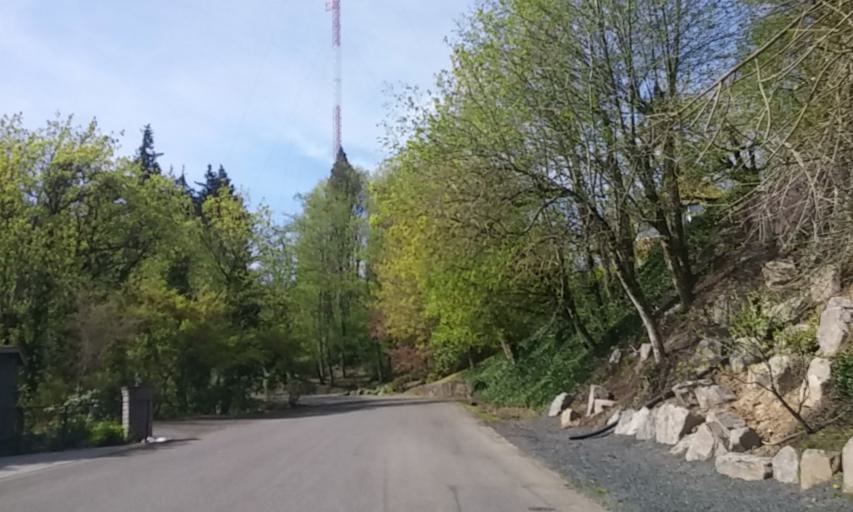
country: US
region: Oregon
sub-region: Washington County
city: West Haven-Sylvan
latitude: 45.5224
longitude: -122.7433
